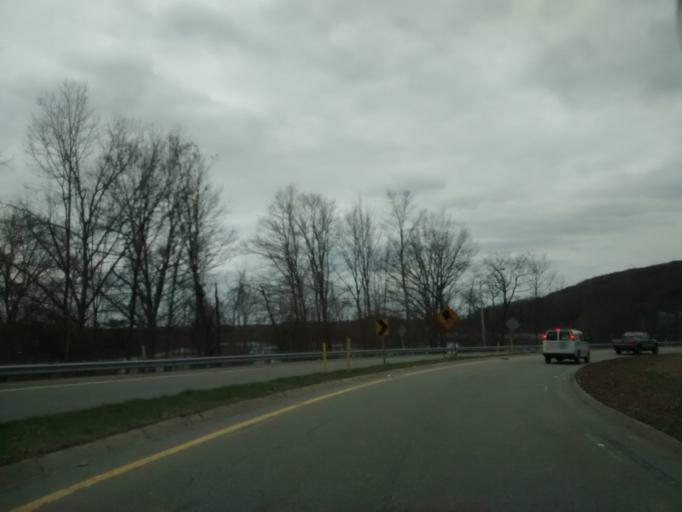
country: US
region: Massachusetts
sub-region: Worcester County
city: Auburn
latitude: 42.1835
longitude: -71.8450
